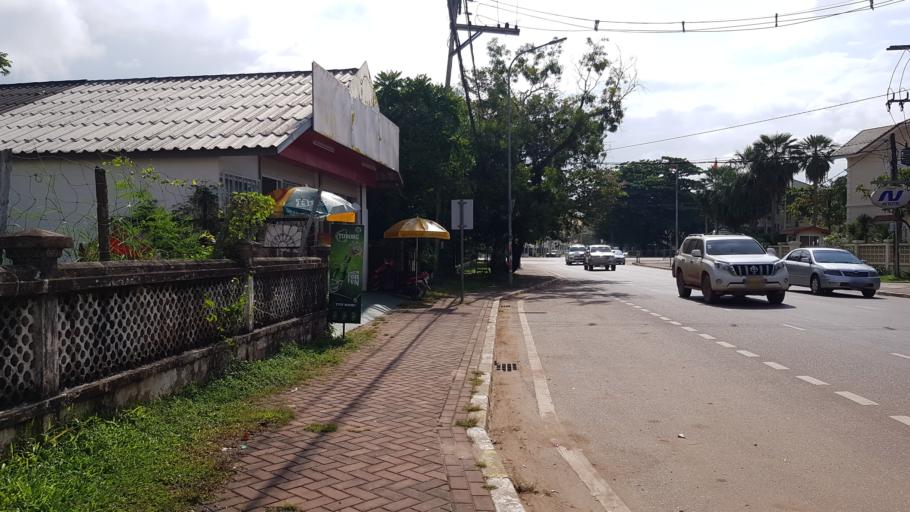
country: LA
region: Vientiane
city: Vientiane
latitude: 17.9649
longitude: 102.6112
